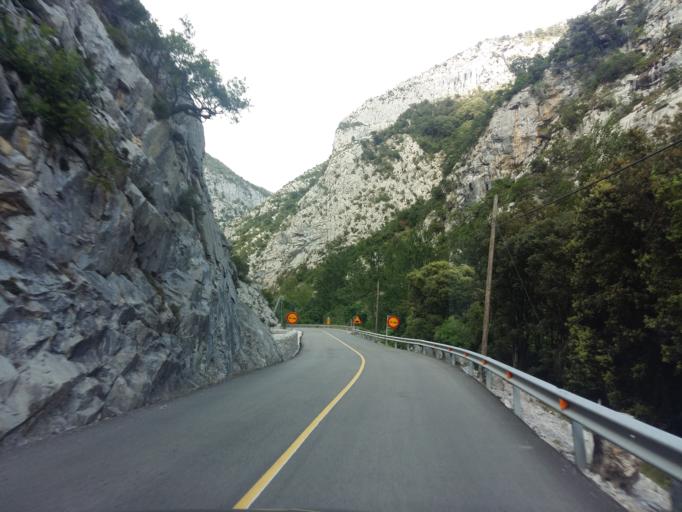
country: ES
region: Cantabria
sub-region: Provincia de Cantabria
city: Potes
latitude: 43.2249
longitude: -4.5853
